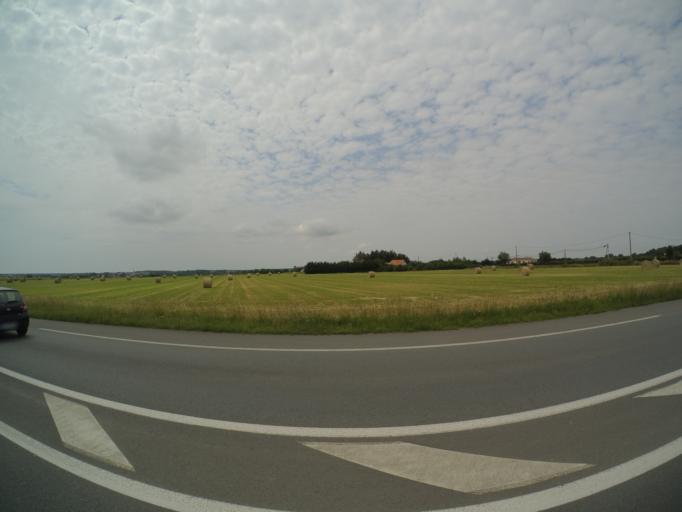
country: FR
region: Pays de la Loire
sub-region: Departement de la Vendee
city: Chavagnes-en-Paillers
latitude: 46.9134
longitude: -1.2410
